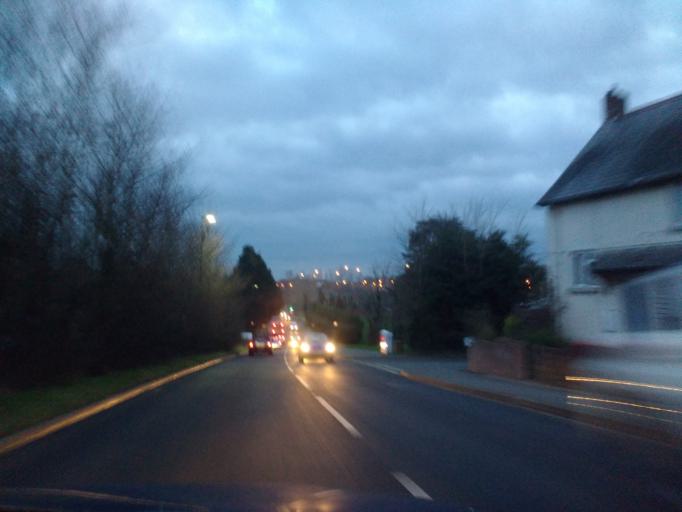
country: GB
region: England
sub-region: Isle of Wight
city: Newport
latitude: 50.7181
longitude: -1.3040
